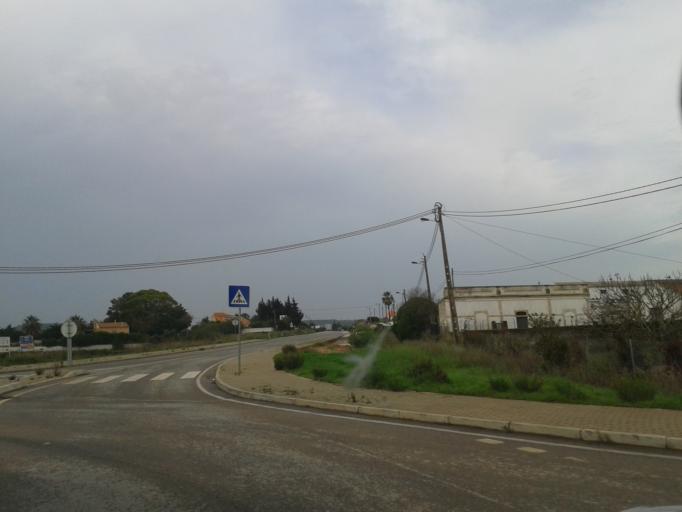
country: PT
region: Faro
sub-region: Lagos
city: Lagos
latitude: 37.0945
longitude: -8.7681
